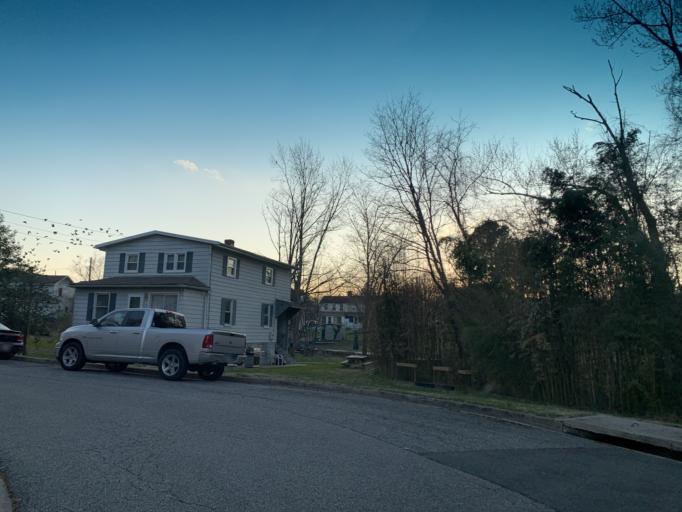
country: US
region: Maryland
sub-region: Harford County
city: Havre de Grace
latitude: 39.5560
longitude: -76.0953
